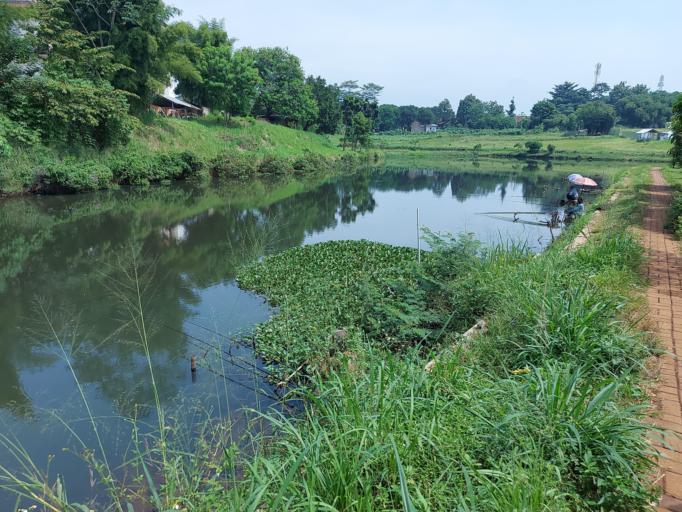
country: ID
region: West Java
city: Cibinong
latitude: -6.4814
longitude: 106.8319
